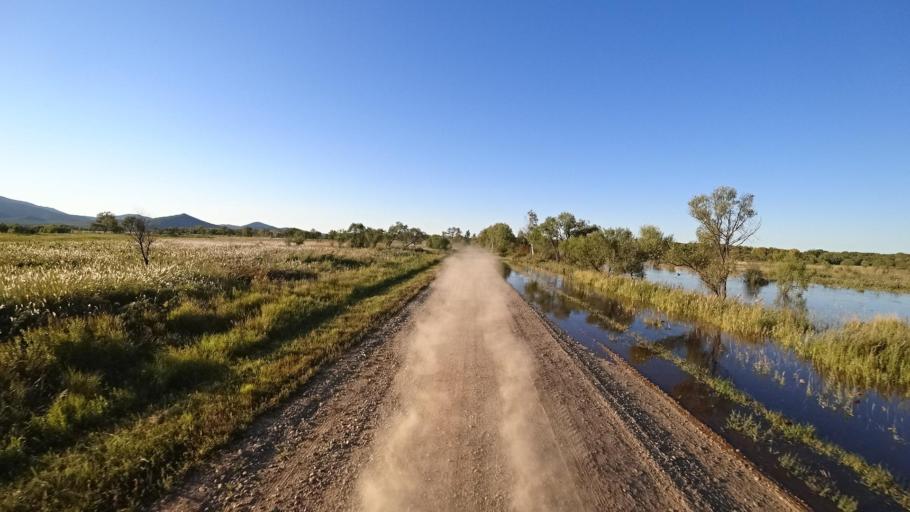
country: RU
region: Primorskiy
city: Kirovskiy
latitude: 44.8115
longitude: 133.6163
